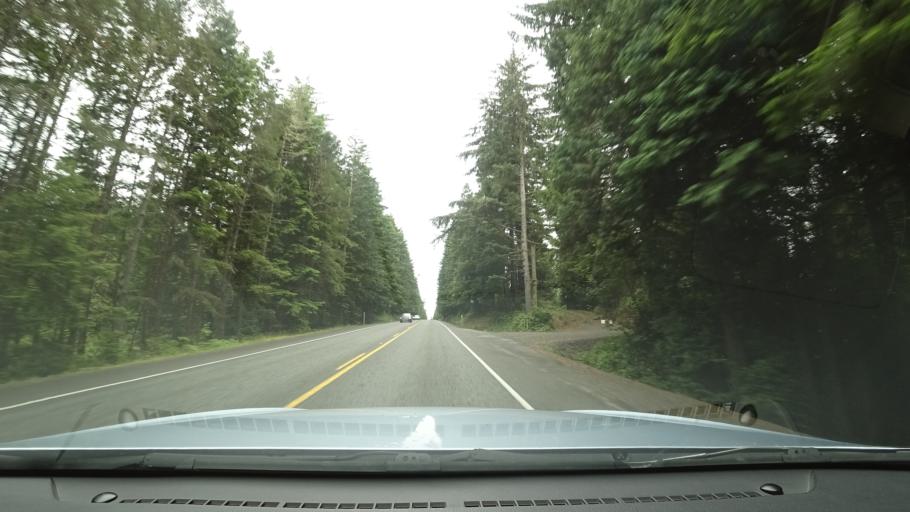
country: US
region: Oregon
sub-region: Coos County
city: Lakeside
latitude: 43.5536
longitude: -124.2091
